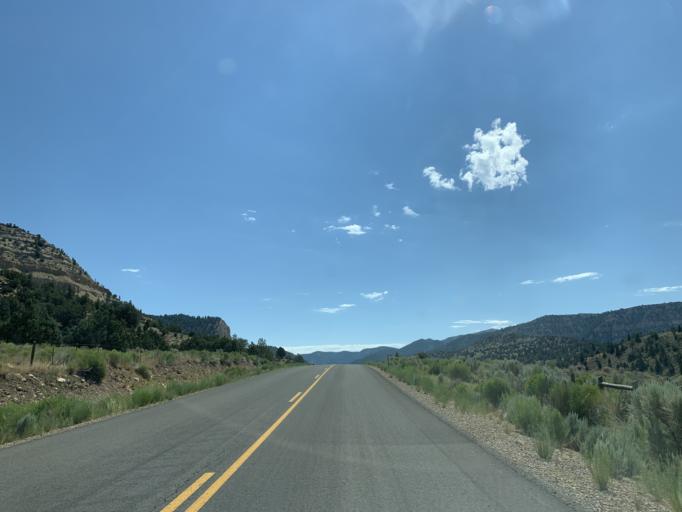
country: US
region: Utah
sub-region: Carbon County
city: East Carbon City
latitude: 39.7762
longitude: -110.4941
